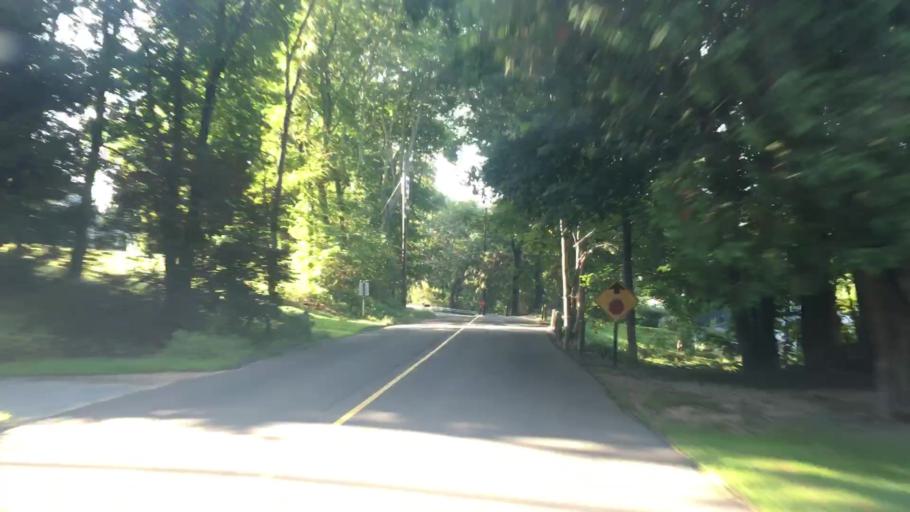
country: US
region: Connecticut
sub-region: Middlesex County
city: Chester Center
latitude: 41.3973
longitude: -72.4547
